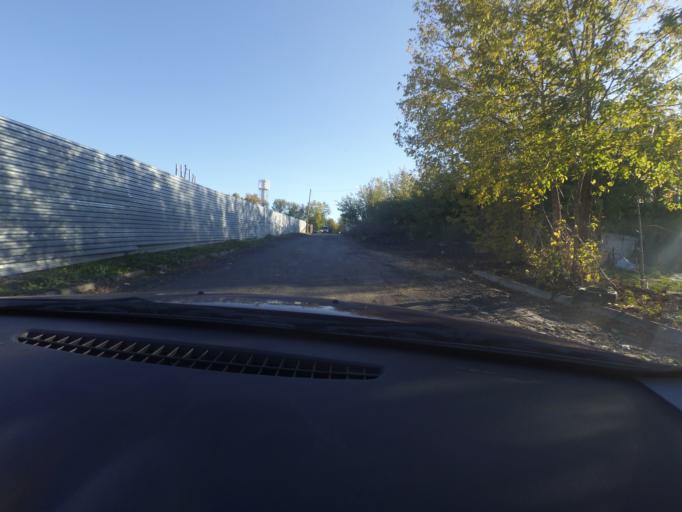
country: RU
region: Nizjnij Novgorod
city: Bor
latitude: 56.3090
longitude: 44.0704
